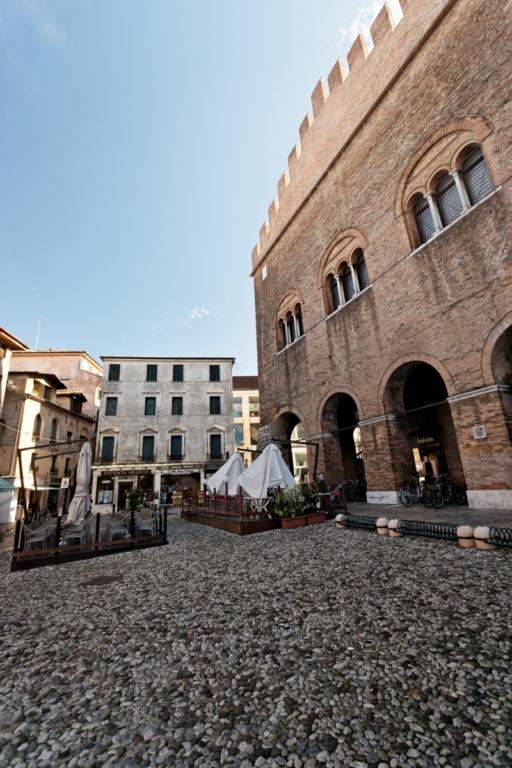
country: IT
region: Veneto
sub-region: Provincia di Treviso
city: Treviso
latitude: 45.6662
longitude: 12.2462
